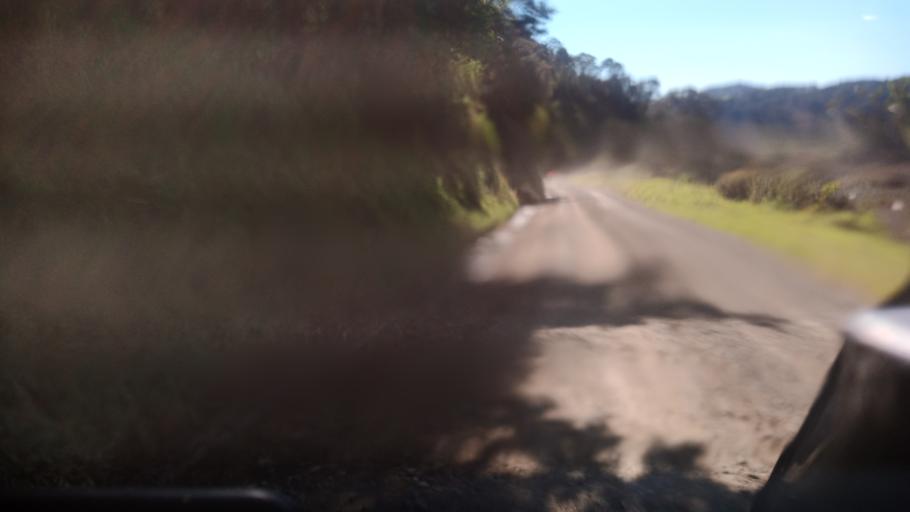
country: NZ
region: Bay of Plenty
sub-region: Opotiki District
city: Opotiki
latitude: -38.0302
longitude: 177.4412
